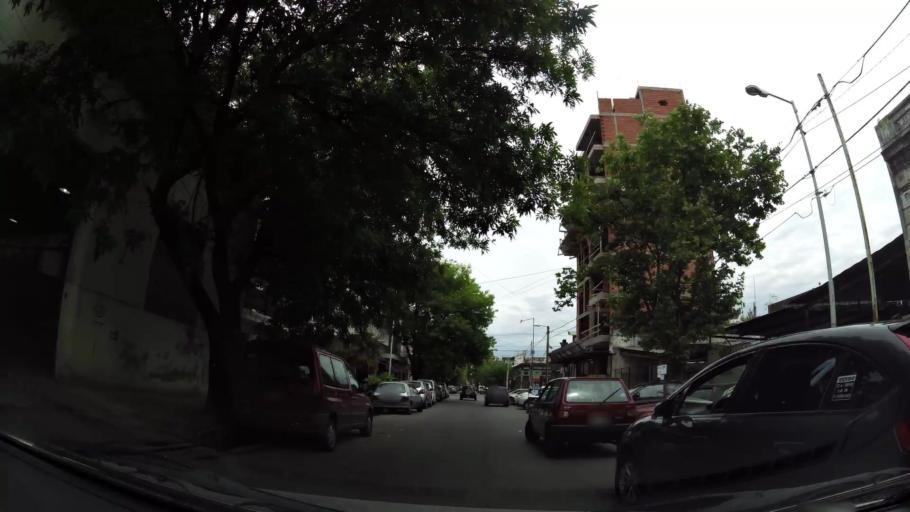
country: AR
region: Buenos Aires
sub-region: Partido de Avellaneda
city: Avellaneda
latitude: -34.6641
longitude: -58.3682
